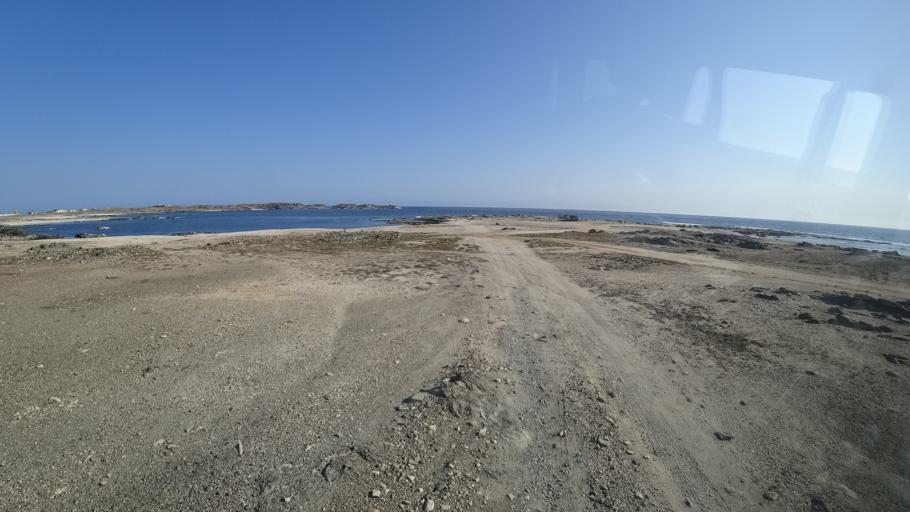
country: OM
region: Zufar
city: Salalah
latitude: 16.9463
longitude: 54.7921
